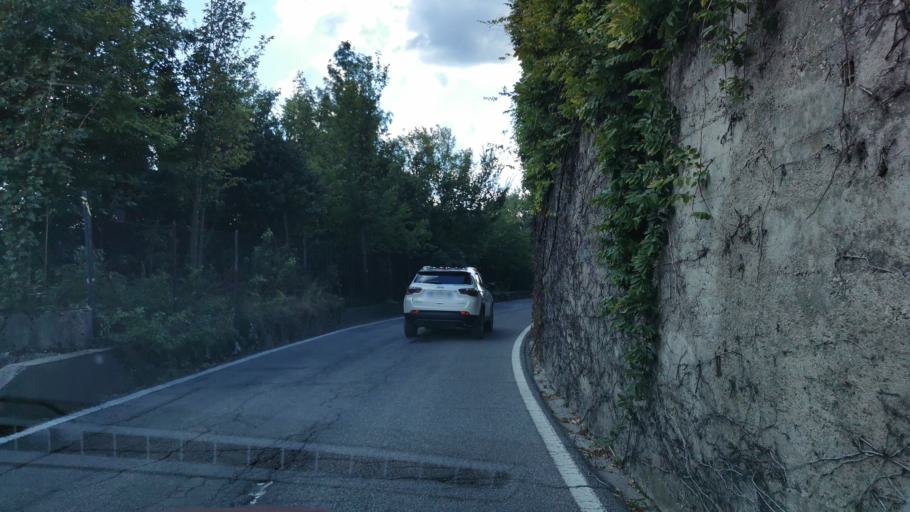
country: IT
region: Lombardy
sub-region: Provincia di Como
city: Cernobbio
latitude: 45.8494
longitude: 9.0840
